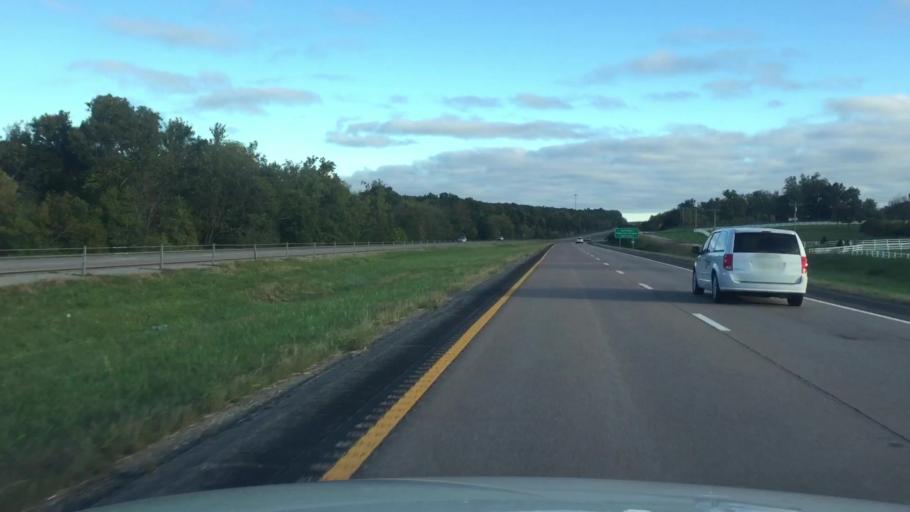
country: US
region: Missouri
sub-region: Boone County
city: Ashland
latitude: 38.8172
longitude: -92.2514
